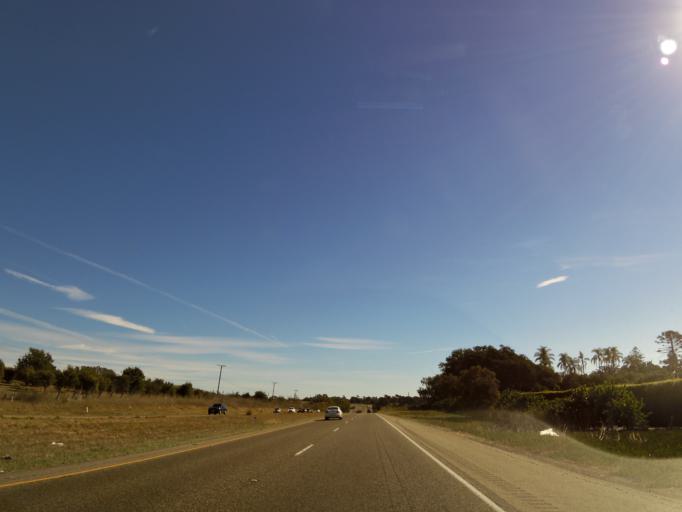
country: US
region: California
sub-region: Santa Barbara County
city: Isla Vista
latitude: 34.4520
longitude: -119.9653
